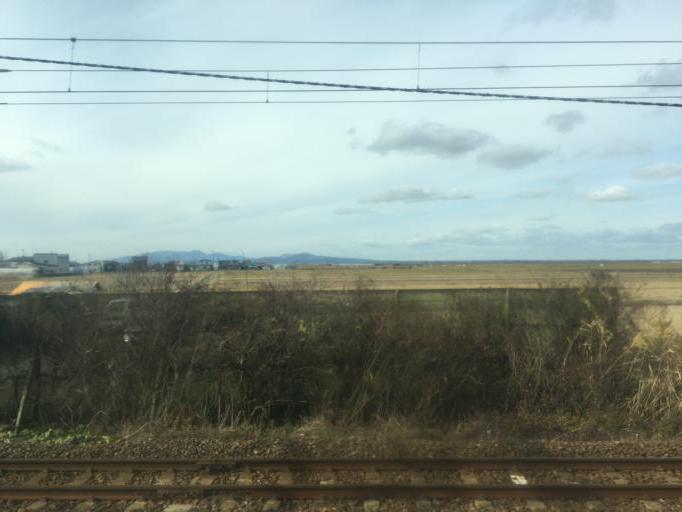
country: JP
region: Akita
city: Tenno
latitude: 39.9012
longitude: 140.0742
